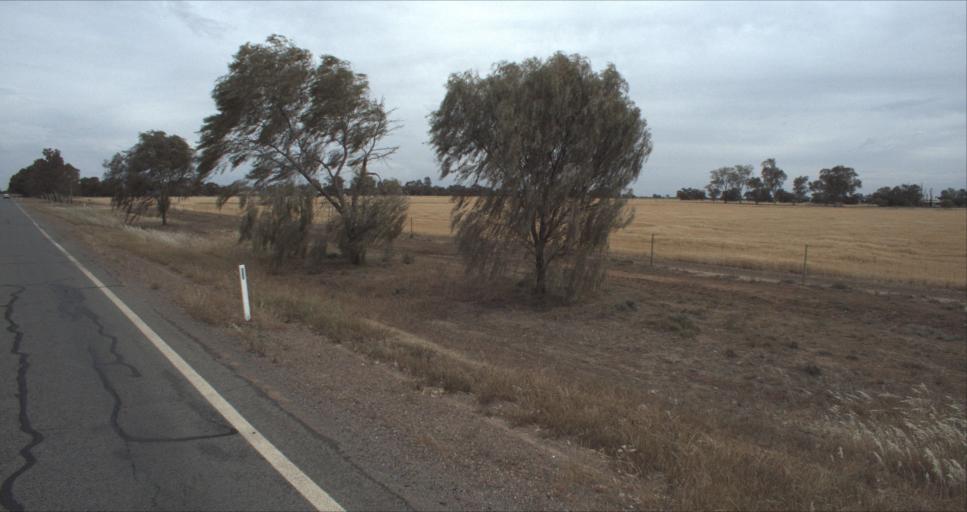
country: AU
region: New South Wales
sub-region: Leeton
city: Leeton
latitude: -34.5160
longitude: 146.4171
